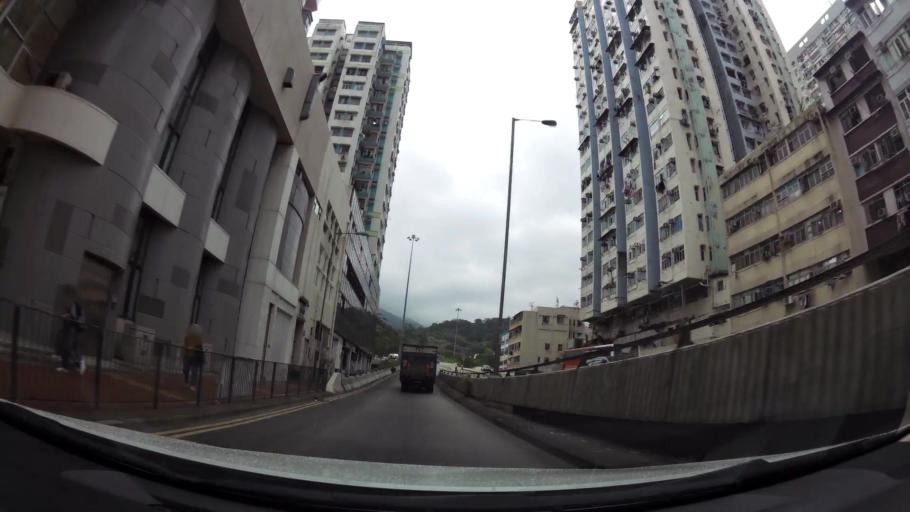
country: HK
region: Tsuen Wan
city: Tsuen Wan
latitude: 22.3689
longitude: 114.1226
